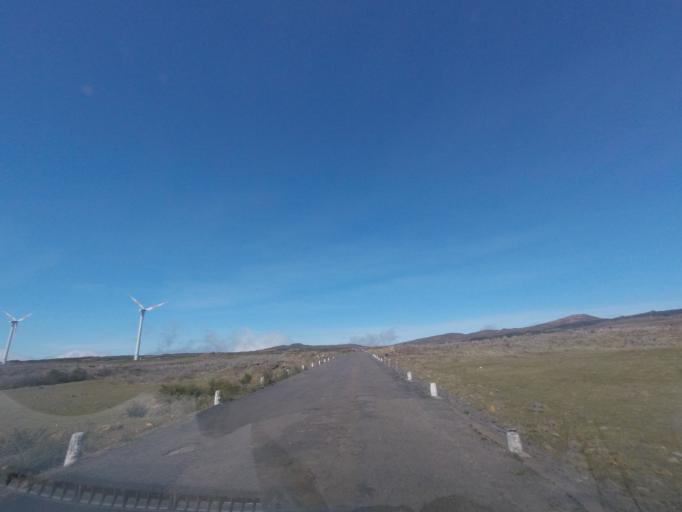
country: PT
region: Madeira
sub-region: Calheta
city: Arco da Calheta
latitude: 32.7428
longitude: -17.0972
